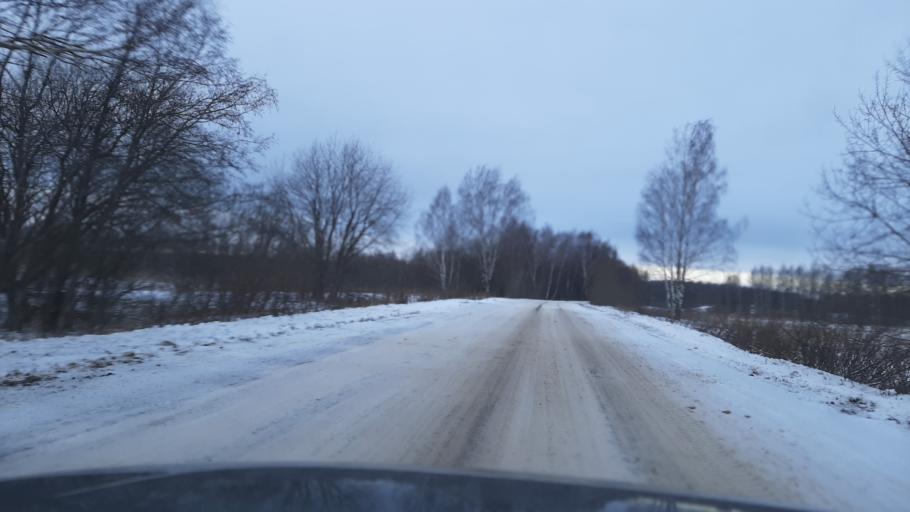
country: RU
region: Kostroma
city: Volgorechensk
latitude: 57.4378
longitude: 41.0485
